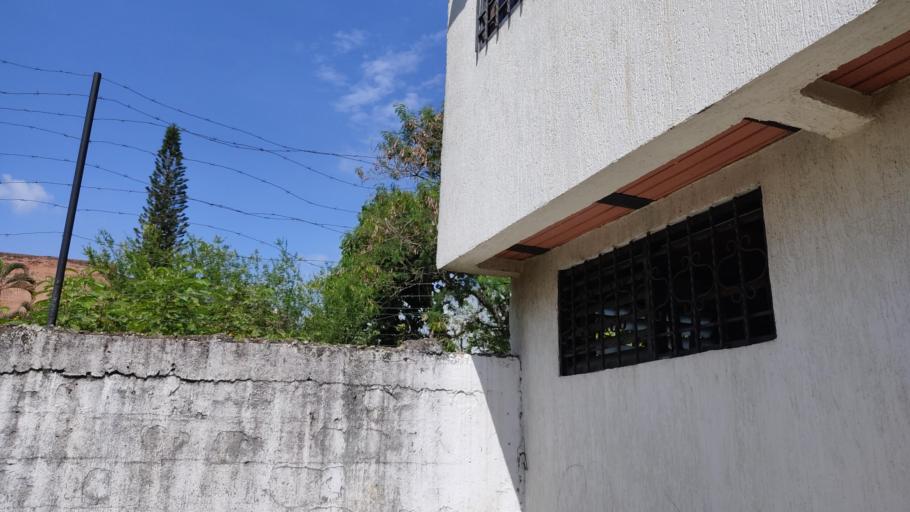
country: CO
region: Valle del Cauca
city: Jamundi
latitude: 3.2544
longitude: -76.5456
